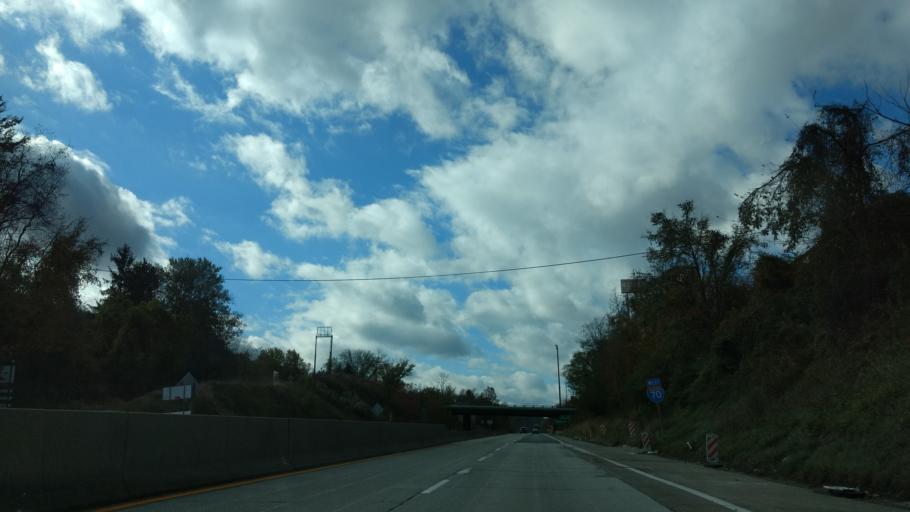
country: US
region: Pennsylvania
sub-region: Washington County
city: Speers
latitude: 40.1209
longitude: -79.8837
